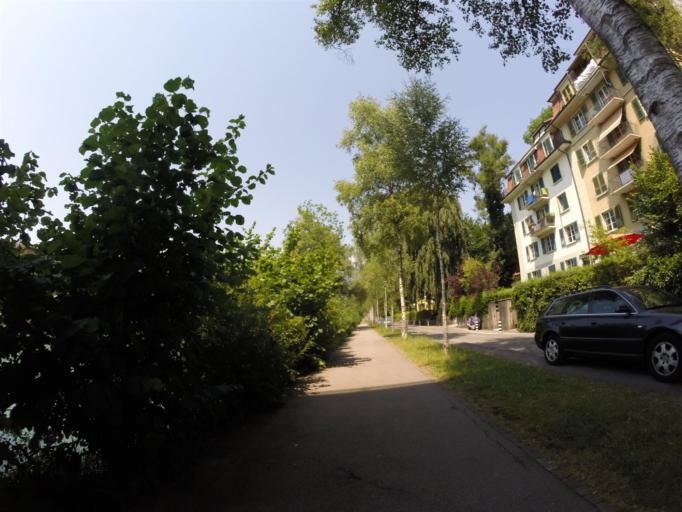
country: CH
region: Bern
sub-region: Bern-Mittelland District
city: Bern
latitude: 46.9400
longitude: 7.4451
